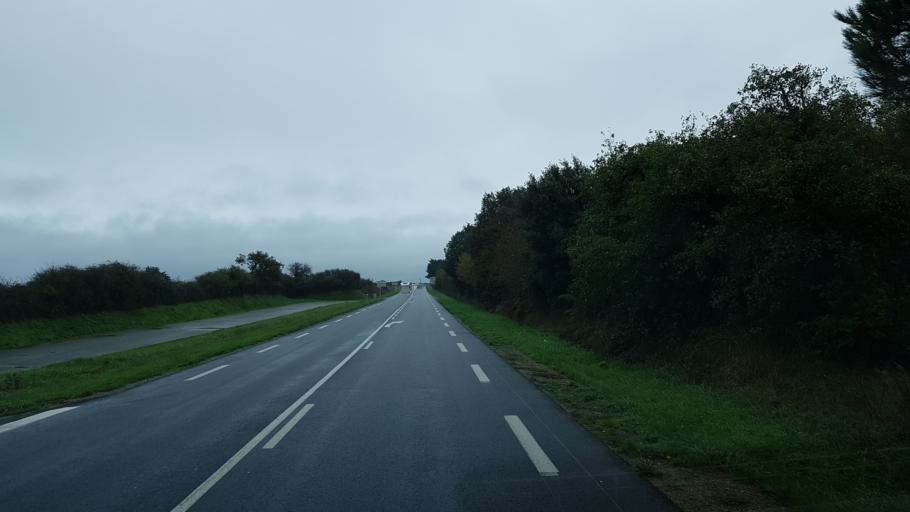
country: FR
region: Brittany
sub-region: Departement du Morbihan
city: Arzon
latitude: 47.5394
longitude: -2.8744
